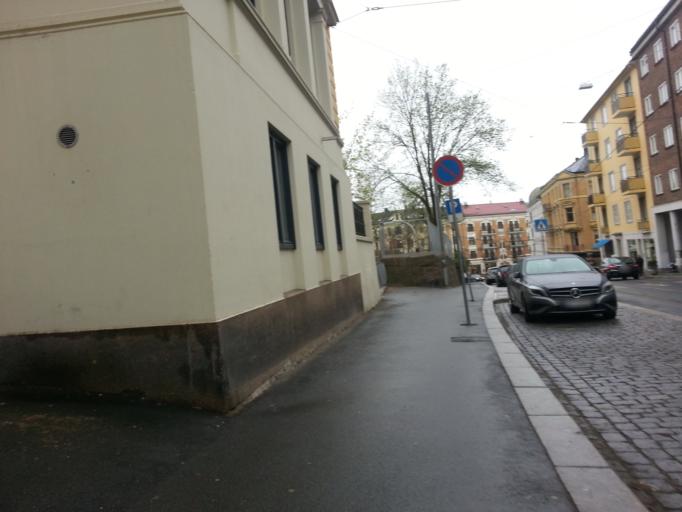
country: NO
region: Oslo
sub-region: Oslo
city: Oslo
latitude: 59.9199
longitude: 10.7183
